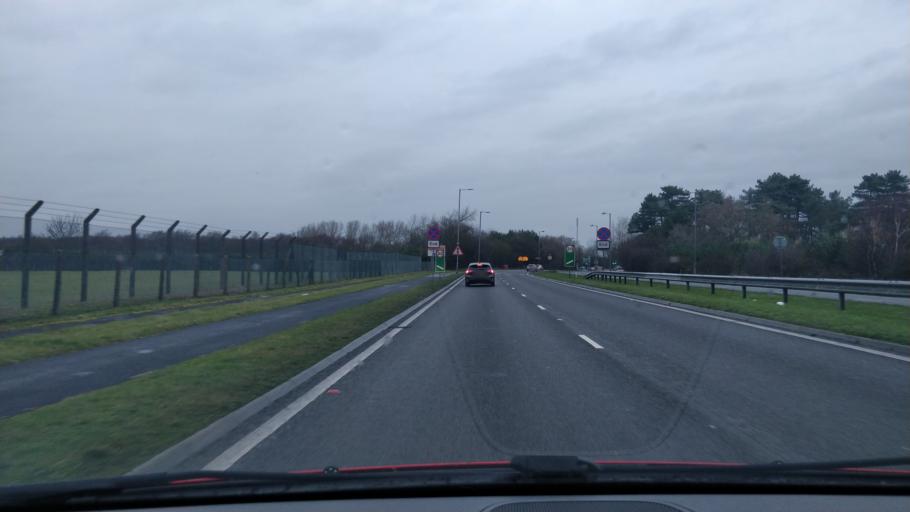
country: GB
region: England
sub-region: Sefton
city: Formby
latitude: 53.5851
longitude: -3.0441
